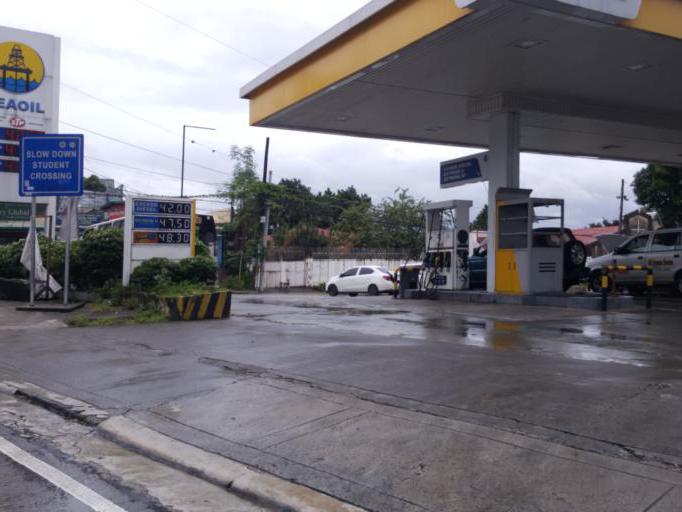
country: PH
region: Calabarzon
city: Bagong Pagasa
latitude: 14.7336
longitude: 121.0526
